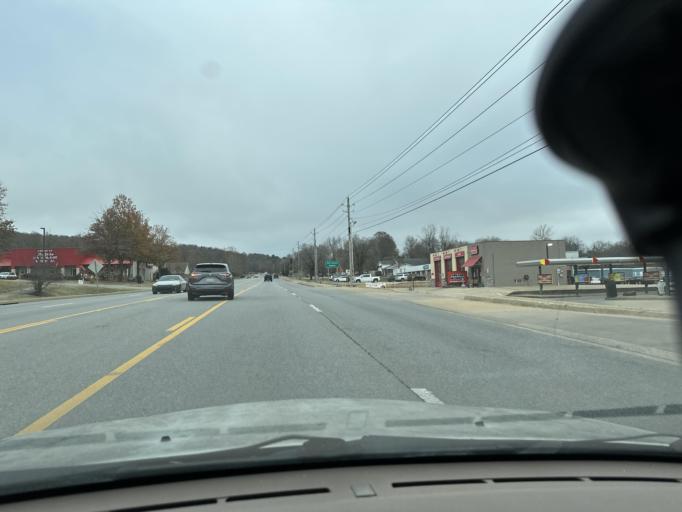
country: US
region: Arkansas
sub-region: Washington County
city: Fayetteville
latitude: 36.0859
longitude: -94.1214
